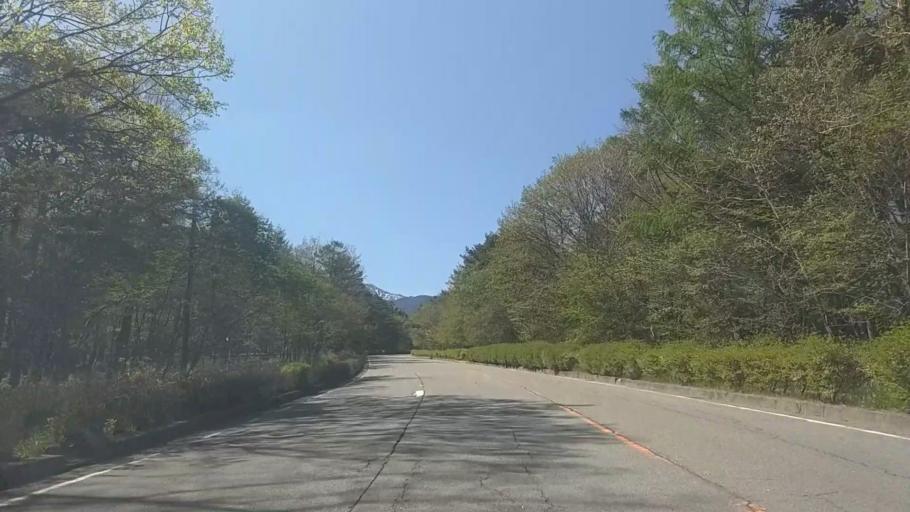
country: JP
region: Yamanashi
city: Nirasaki
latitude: 35.9306
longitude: 138.4279
